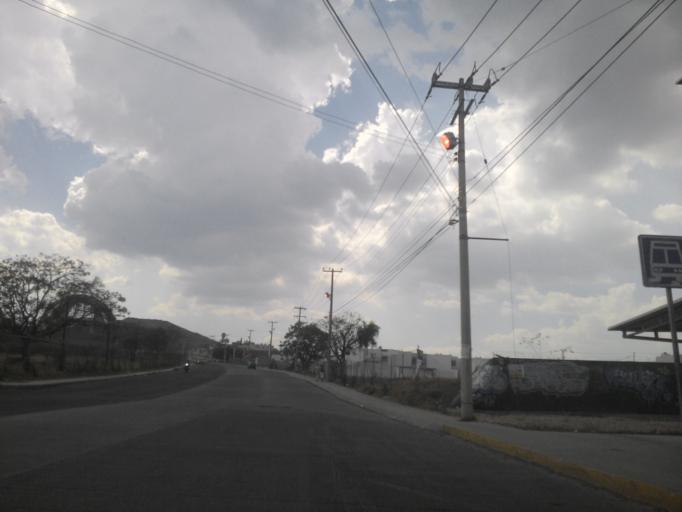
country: MX
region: Jalisco
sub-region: San Pedro Tlaquepaque
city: Paseo del Prado
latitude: 20.6137
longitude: -103.3971
